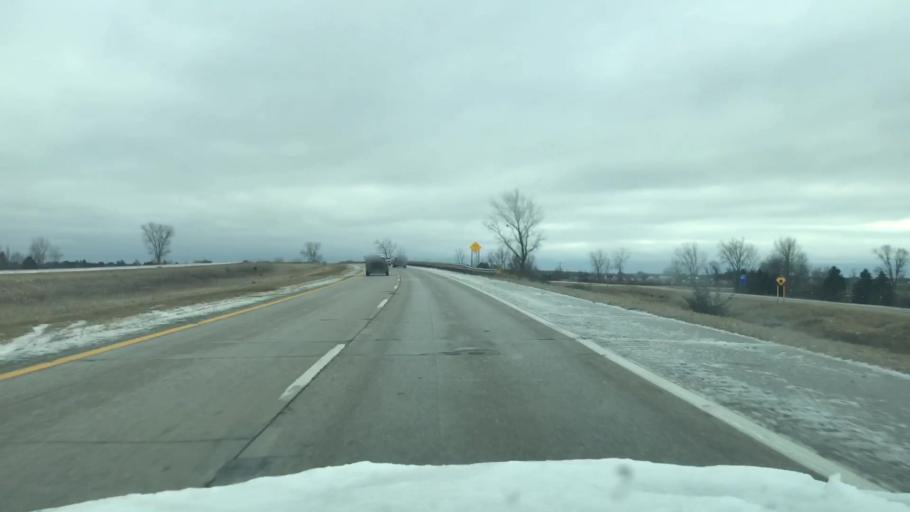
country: US
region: Michigan
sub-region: Bay County
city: Auburn
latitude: 43.6734
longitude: -84.0134
